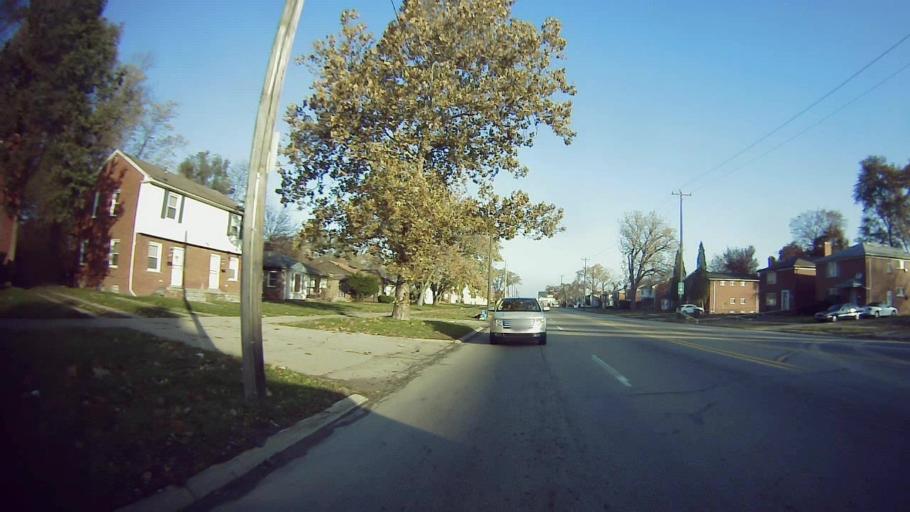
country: US
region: Michigan
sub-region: Oakland County
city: Oak Park
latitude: 42.4381
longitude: -83.2003
